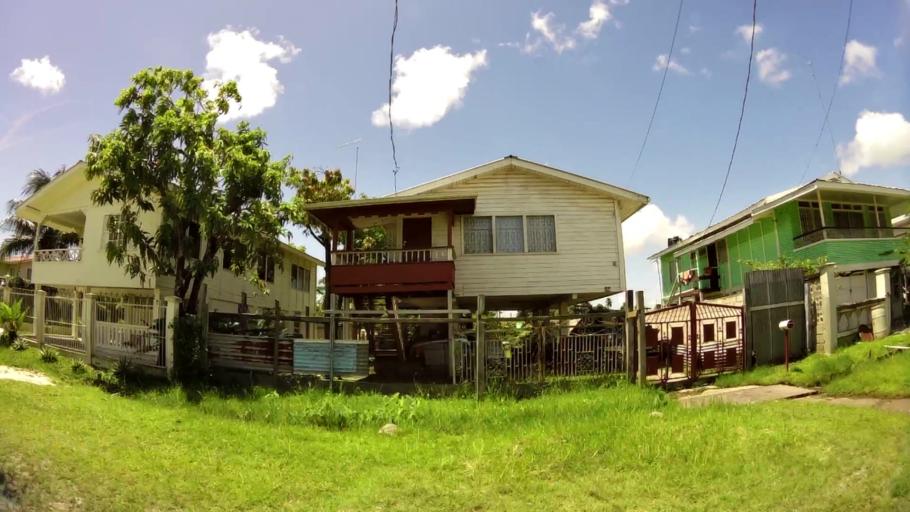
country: GY
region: Demerara-Mahaica
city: Georgetown
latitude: 6.7864
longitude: -58.1499
